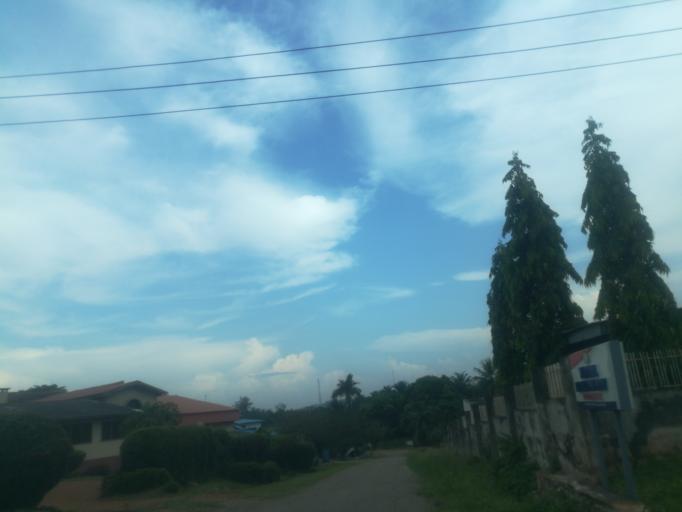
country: NG
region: Oyo
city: Ibadan
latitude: 7.4171
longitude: 3.9068
